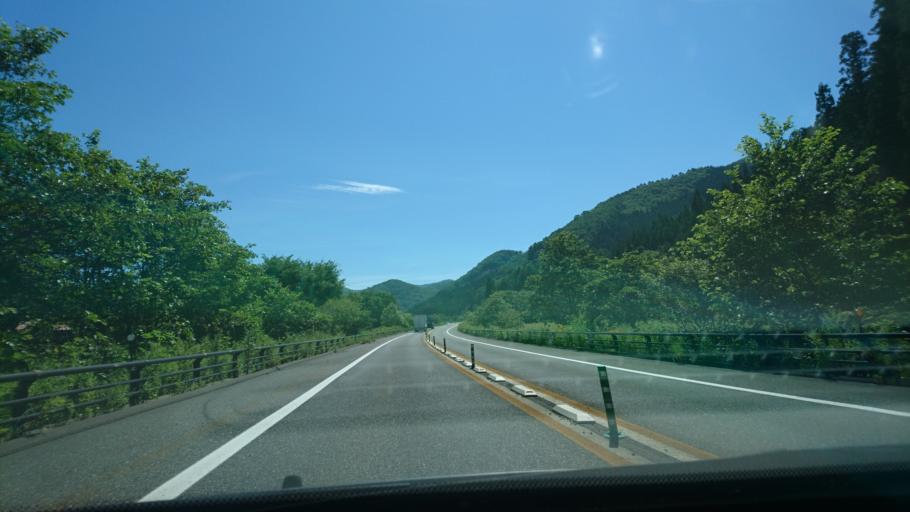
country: JP
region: Iwate
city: Tono
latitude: 39.2618
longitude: 141.6137
